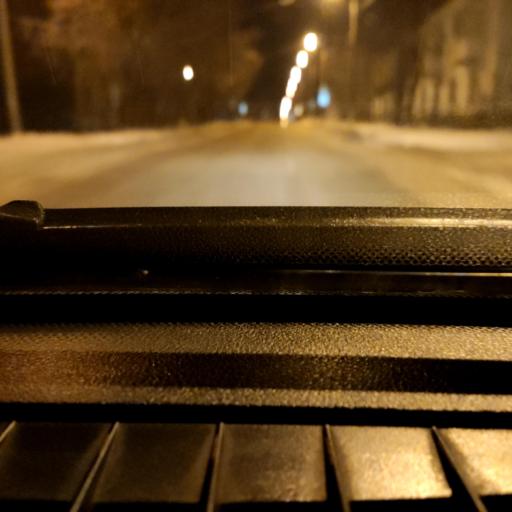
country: RU
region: Perm
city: Perm
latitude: 58.0877
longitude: 56.3890
